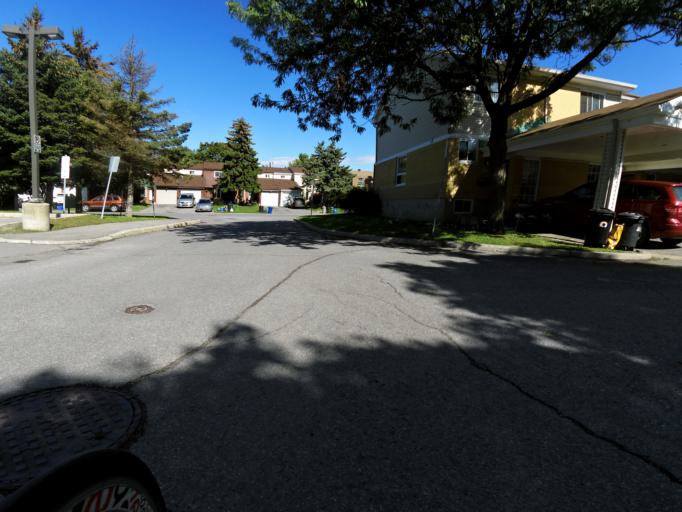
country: CA
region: Ontario
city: Bells Corners
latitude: 45.3170
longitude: -75.8364
